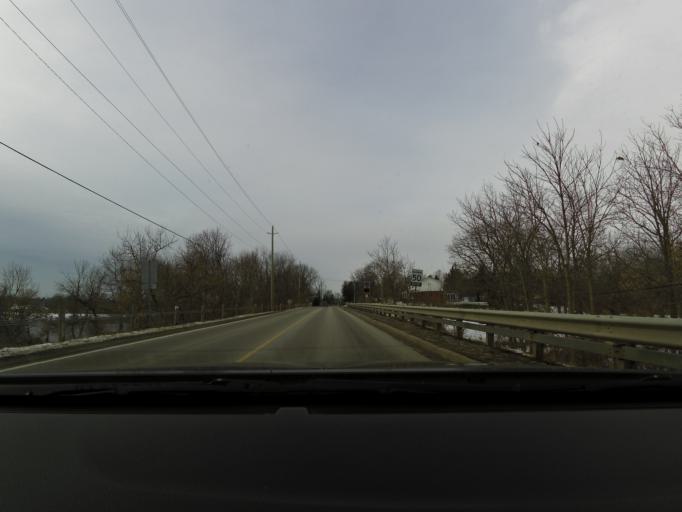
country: CA
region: Ontario
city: Ancaster
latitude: 43.0654
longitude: -79.9343
